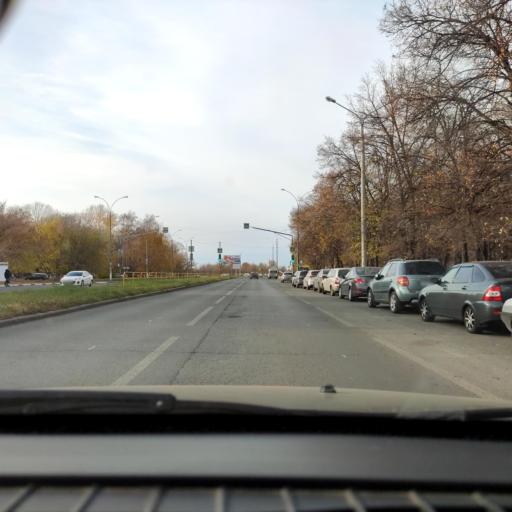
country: RU
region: Samara
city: Tol'yatti
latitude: 53.5164
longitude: 49.2627
